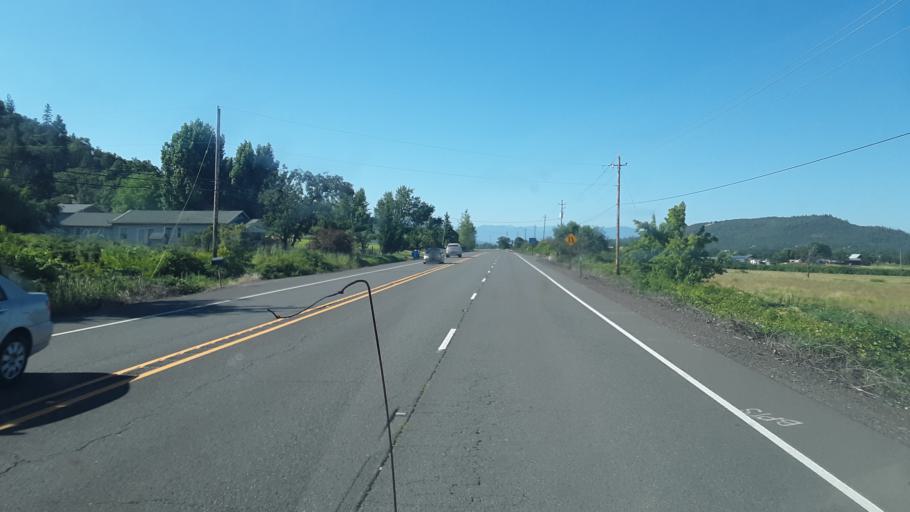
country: US
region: Oregon
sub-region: Jackson County
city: Eagle Point
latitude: 42.5296
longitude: -122.8145
